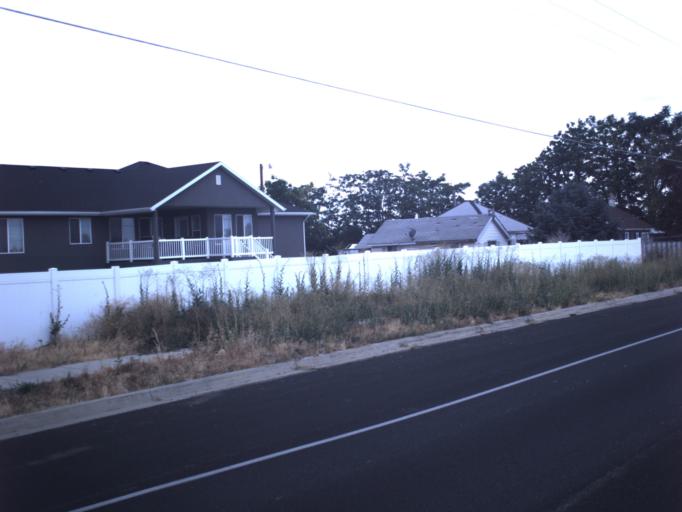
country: US
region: Utah
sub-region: Davis County
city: West Point
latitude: 41.0893
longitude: -112.0971
